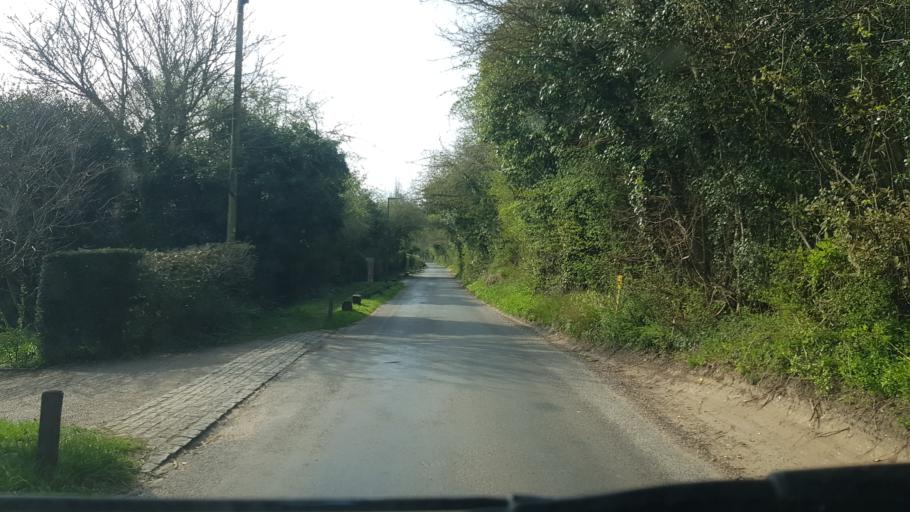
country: GB
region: England
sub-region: Surrey
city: Chilworth
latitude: 51.2318
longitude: -0.5332
